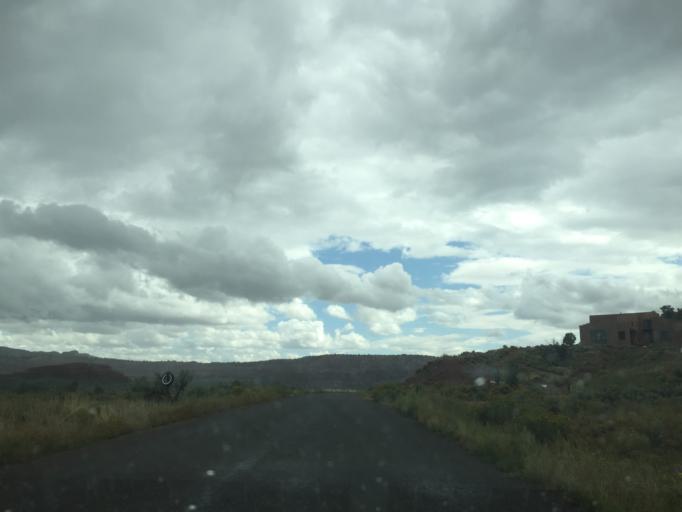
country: US
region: Utah
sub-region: Garfield County
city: Panguitch
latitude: 37.5535
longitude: -112.0494
